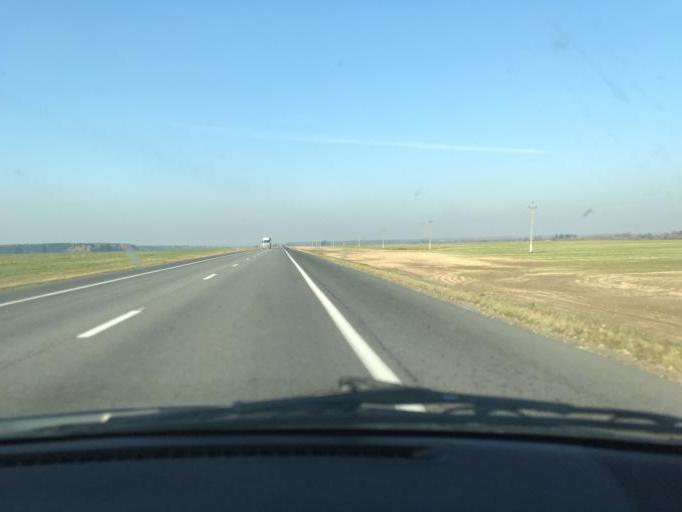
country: BY
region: Vitebsk
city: Orsha
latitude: 54.3527
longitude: 30.4457
